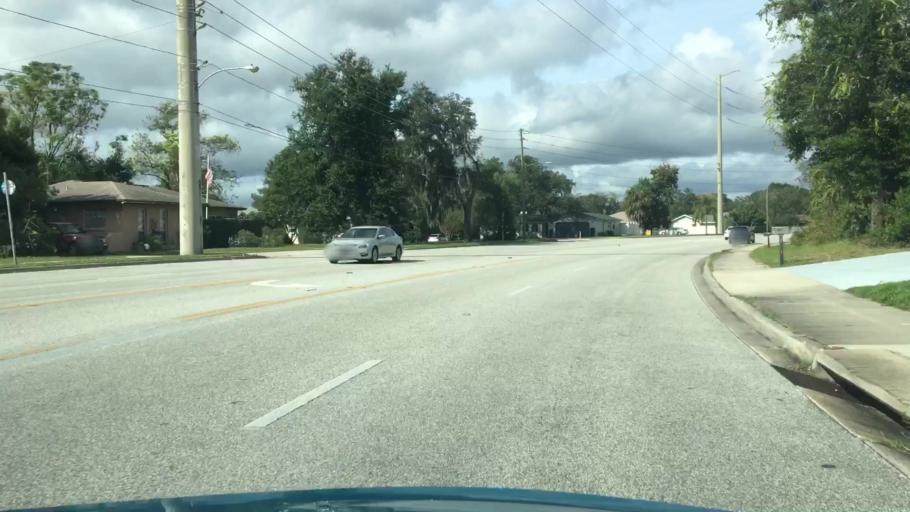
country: US
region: Florida
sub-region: Volusia County
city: Deltona
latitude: 28.9031
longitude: -81.2445
